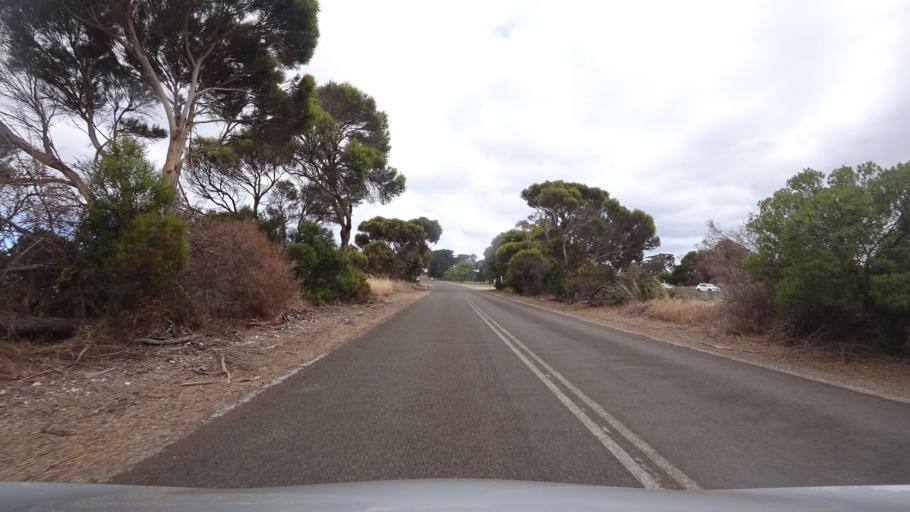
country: AU
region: South Australia
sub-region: Kangaroo Island
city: Kingscote
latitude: -35.6073
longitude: 137.5223
